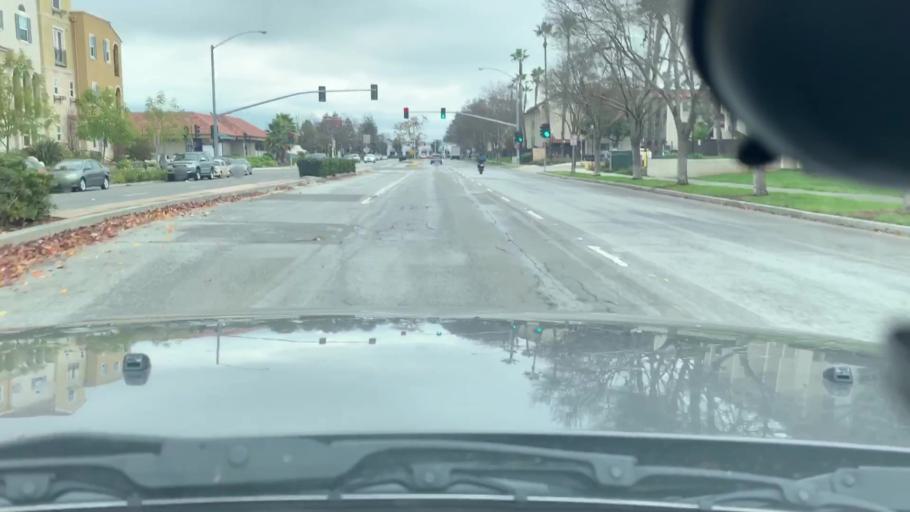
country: US
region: California
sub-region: Alameda County
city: Fremont
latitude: 37.5196
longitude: -121.9944
